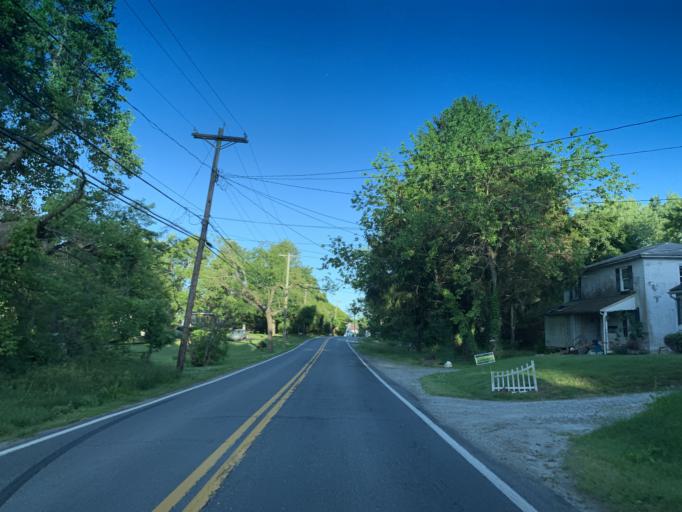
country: US
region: Maryland
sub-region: Cecil County
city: Elkton
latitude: 39.6624
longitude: -75.8315
